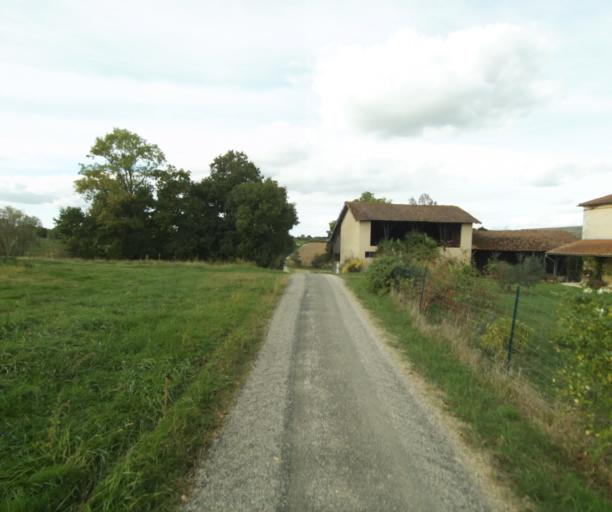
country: FR
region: Midi-Pyrenees
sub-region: Departement du Gers
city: Gondrin
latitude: 43.8381
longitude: 0.1779
